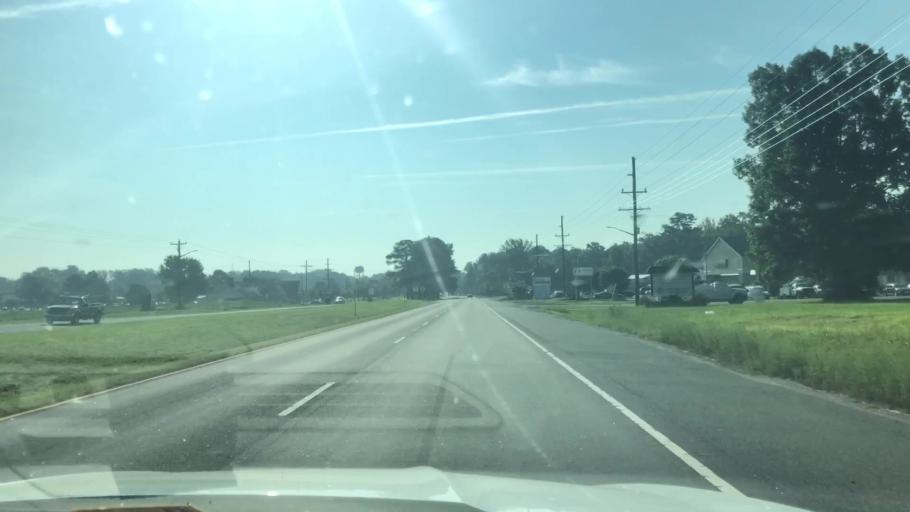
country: US
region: Virginia
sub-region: Richmond County
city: Warsaw
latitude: 37.9632
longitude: -76.7818
